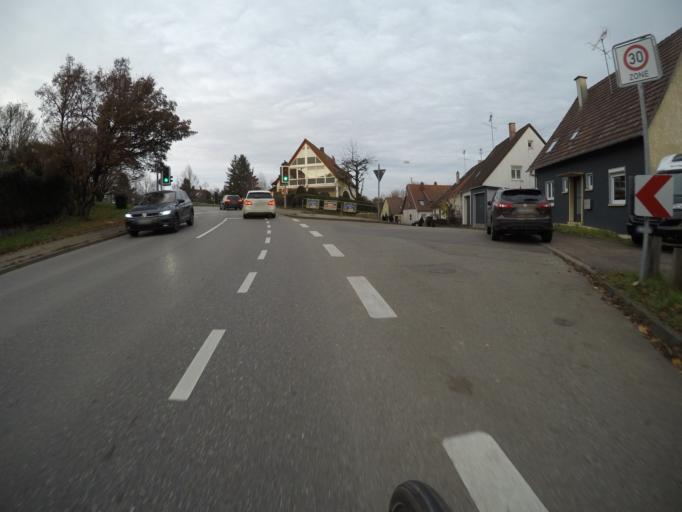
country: DE
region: Baden-Wuerttemberg
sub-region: Regierungsbezirk Stuttgart
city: Neuhausen auf den Fildern
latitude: 48.7085
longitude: 9.2714
